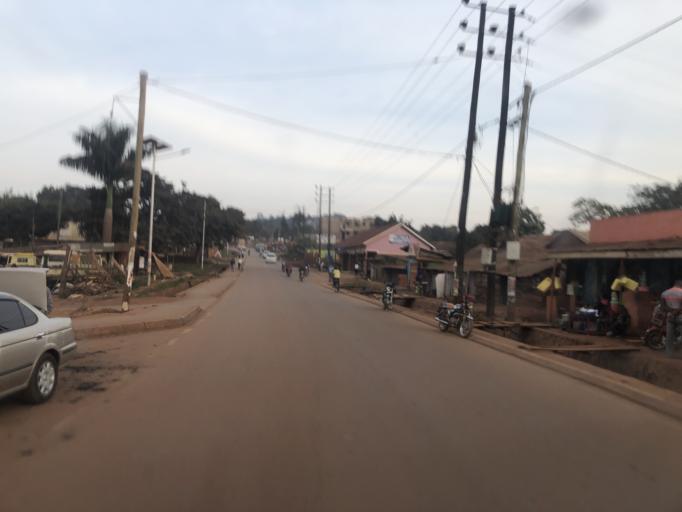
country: UG
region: Central Region
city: Kampala Central Division
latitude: 0.2959
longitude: 32.5272
